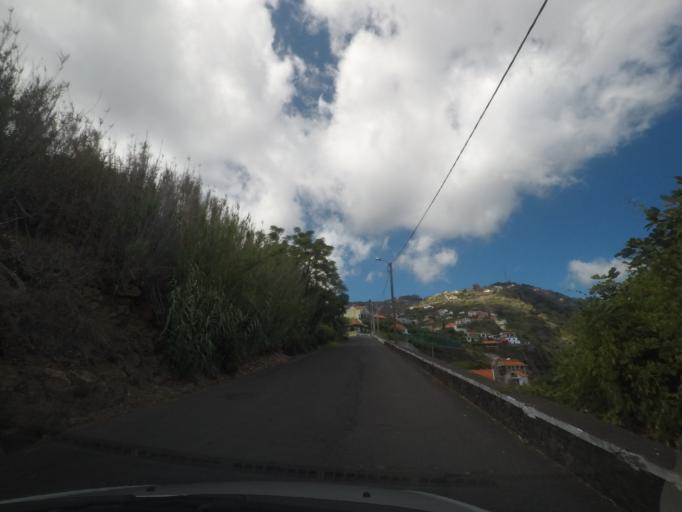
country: PT
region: Madeira
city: Ribeira Brava
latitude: 32.6745
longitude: -17.0663
